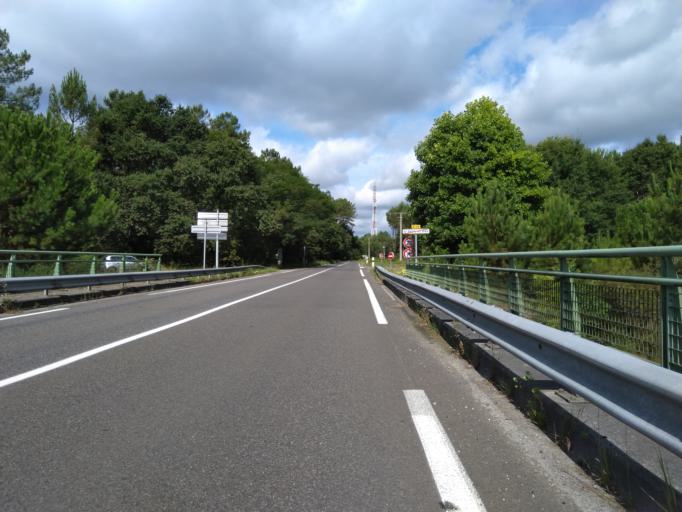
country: FR
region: Aquitaine
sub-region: Departement des Landes
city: Mees
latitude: 43.7326
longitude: -1.1023
